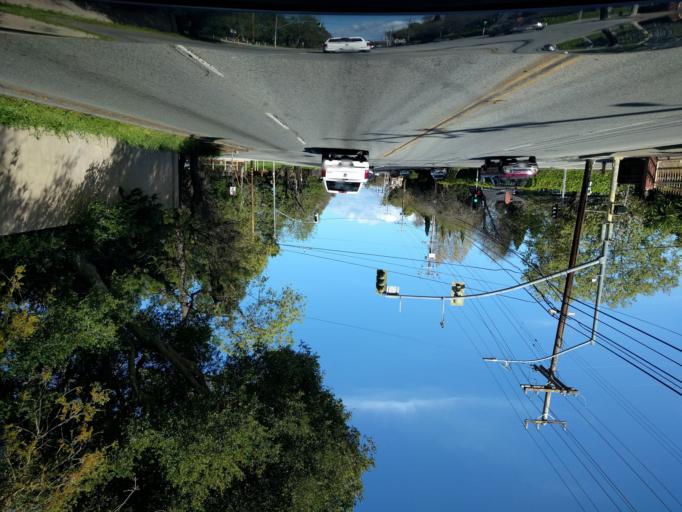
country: US
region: California
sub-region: San Mateo County
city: North Fair Oaks
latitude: 37.4764
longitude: -122.1869
